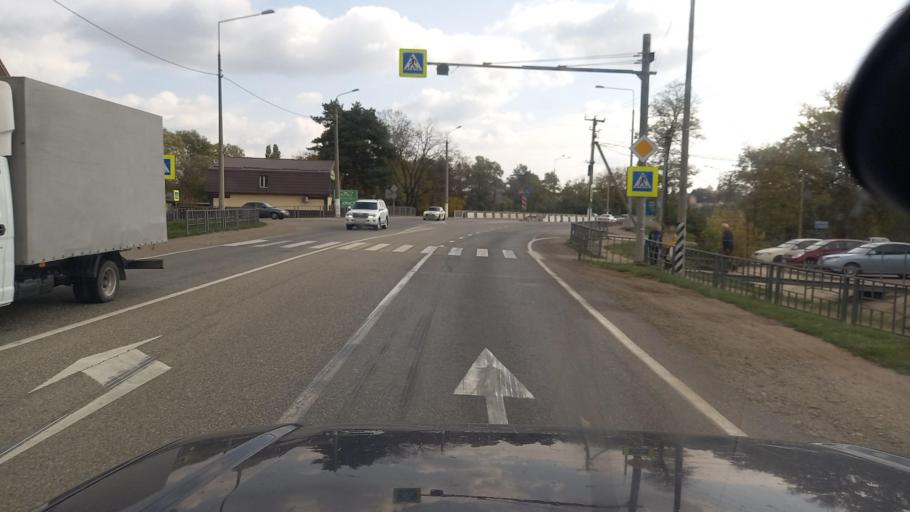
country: RU
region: Krasnodarskiy
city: Kholmskiy
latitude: 44.8452
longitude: 38.3896
